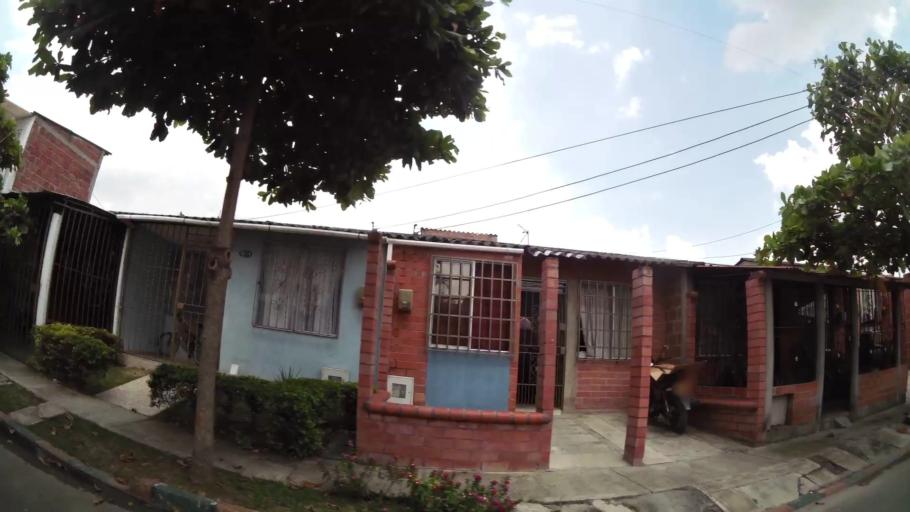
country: CO
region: Valle del Cauca
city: Cali
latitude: 3.4560
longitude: -76.4656
